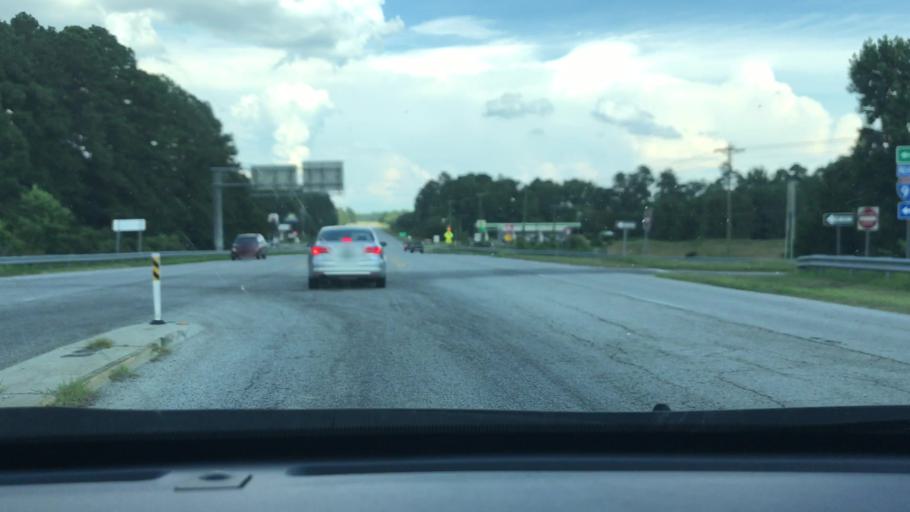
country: US
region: South Carolina
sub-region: Sumter County
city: East Sumter
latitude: 33.9009
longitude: -80.0922
